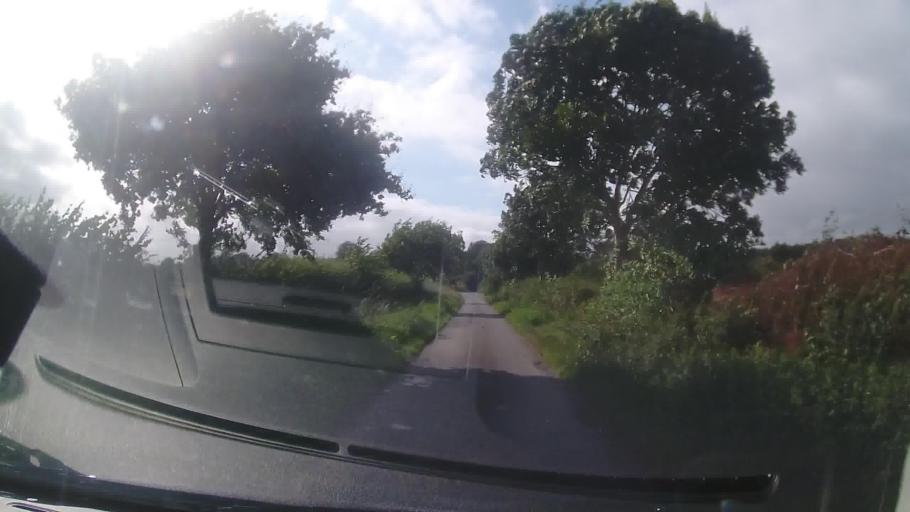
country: GB
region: England
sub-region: Shropshire
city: Bishop's Castle
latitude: 52.4957
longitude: -2.9860
